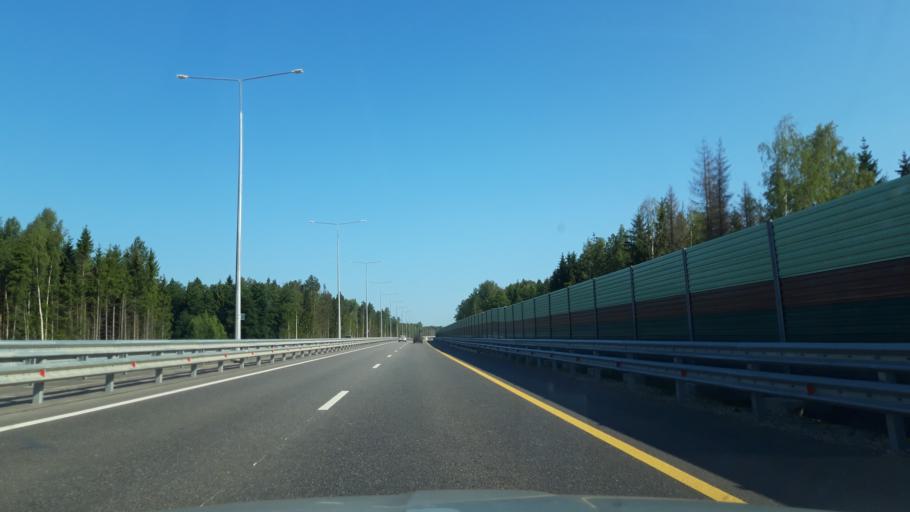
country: RU
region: Moskovskaya
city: Reshetnikovo
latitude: 56.4355
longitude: 36.5446
